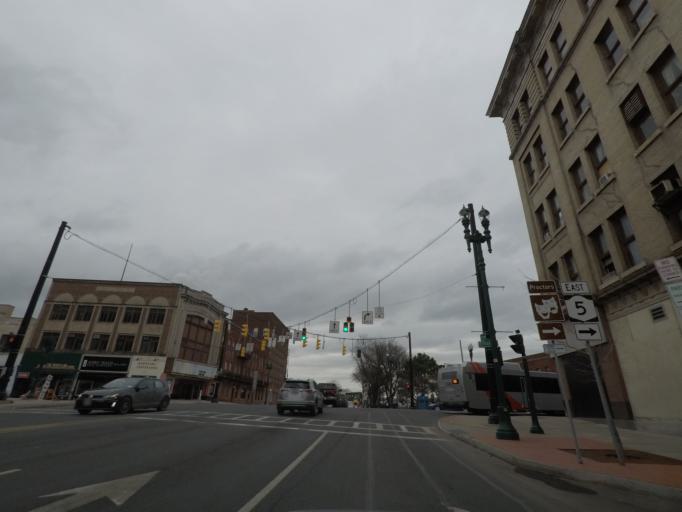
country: US
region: New York
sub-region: Schenectady County
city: Schenectady
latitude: 42.8140
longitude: -73.9443
